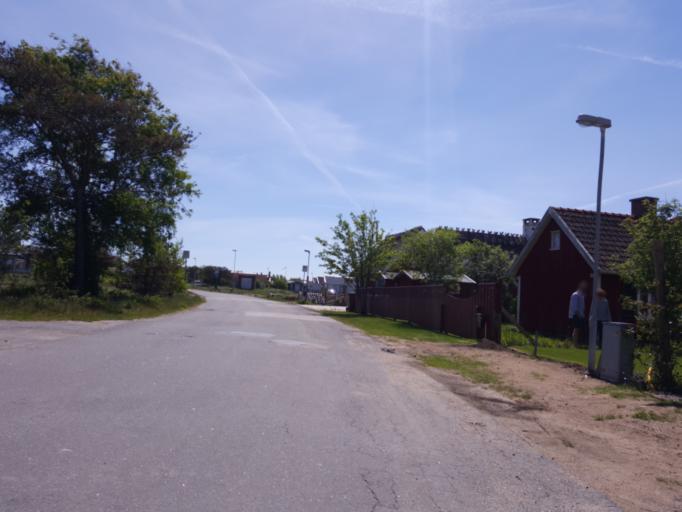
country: SE
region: Halland
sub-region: Falkenbergs Kommun
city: Falkenberg
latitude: 56.8790
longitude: 12.5163
